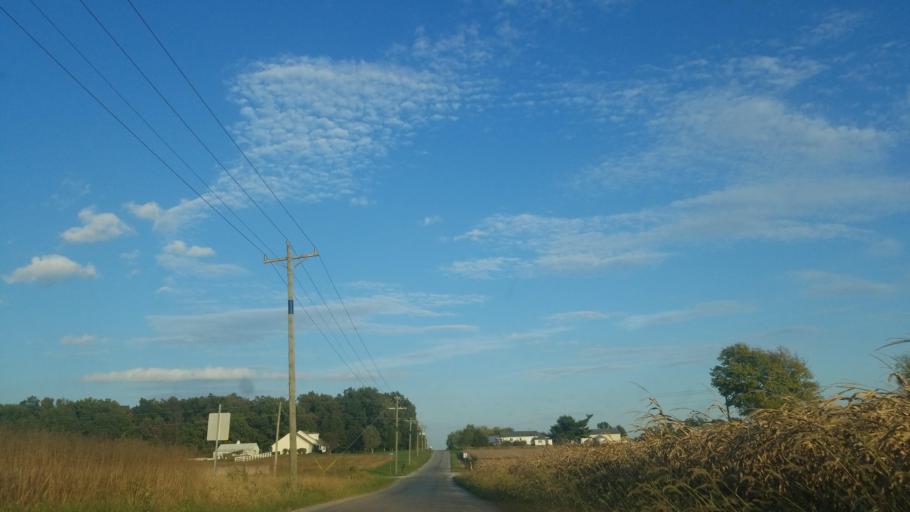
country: US
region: Illinois
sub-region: Saline County
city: Harrisburg
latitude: 37.8048
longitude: -88.6251
